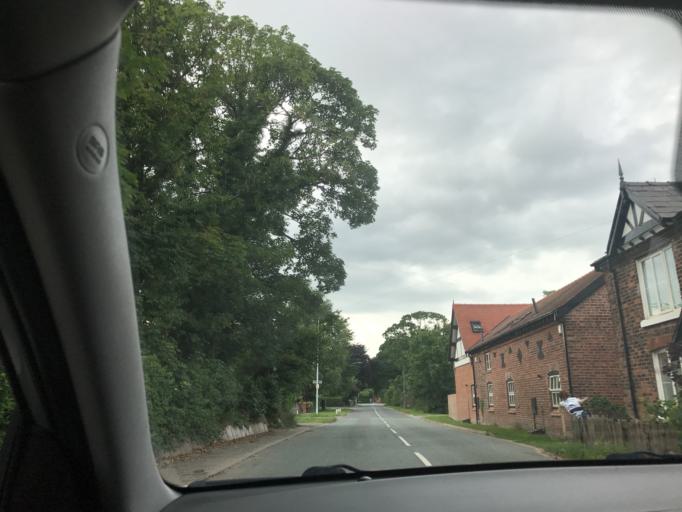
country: GB
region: England
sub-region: Cheshire West and Chester
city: Winsford
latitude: 53.2210
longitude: -2.5097
